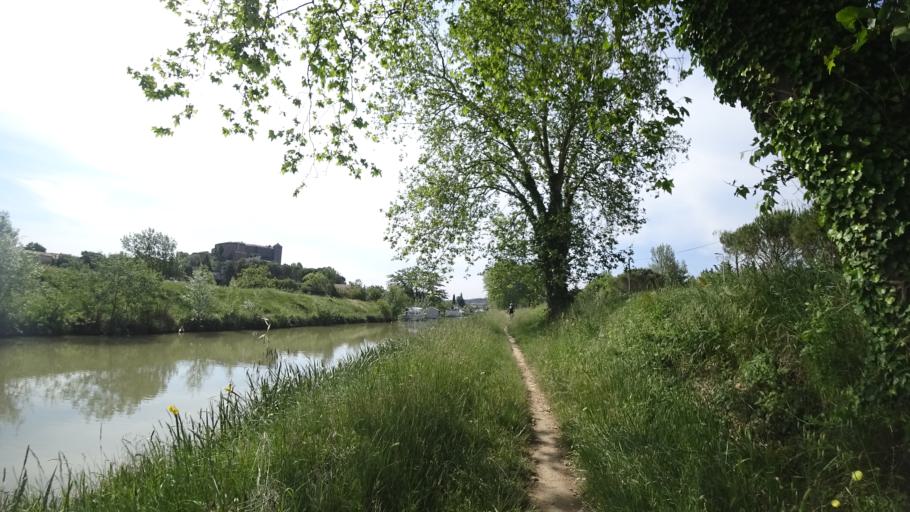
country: FR
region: Languedoc-Roussillon
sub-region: Departement de l'Aude
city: Lezignan-Corbieres
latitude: 43.2439
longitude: 2.7629
